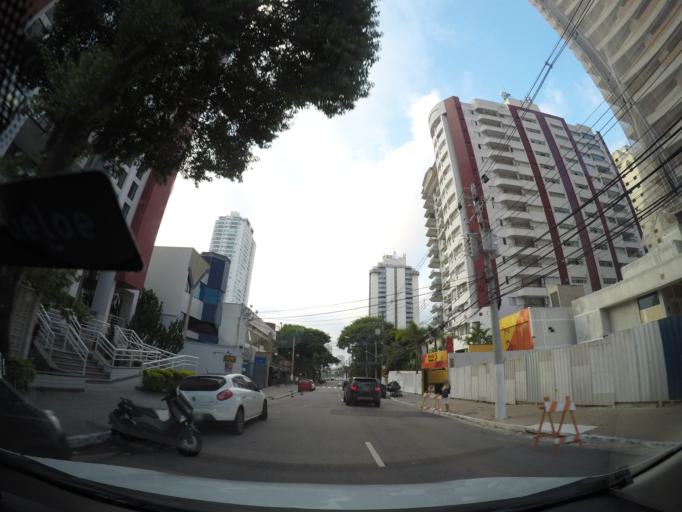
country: BR
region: Sao Paulo
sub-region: Sao Paulo
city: Sao Paulo
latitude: -23.5413
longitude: -46.5672
